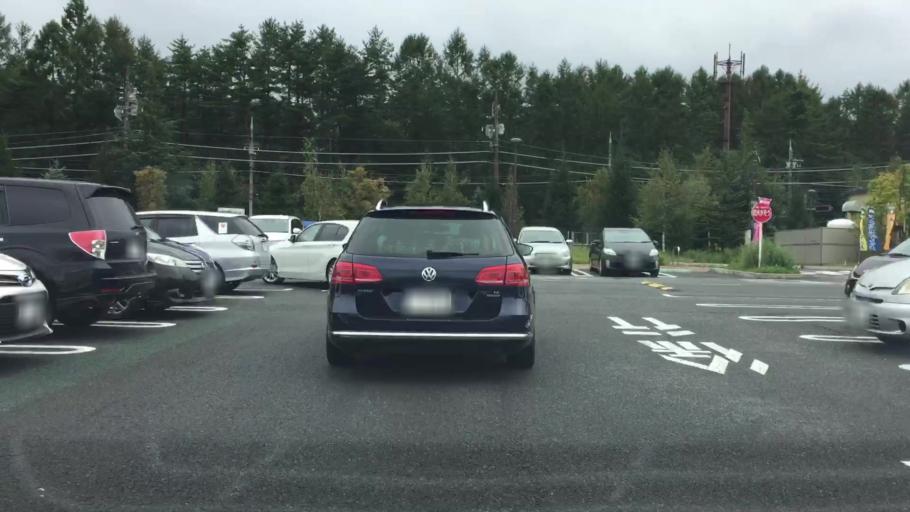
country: JP
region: Yamanashi
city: Fujikawaguchiko
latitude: 35.4904
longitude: 138.7432
